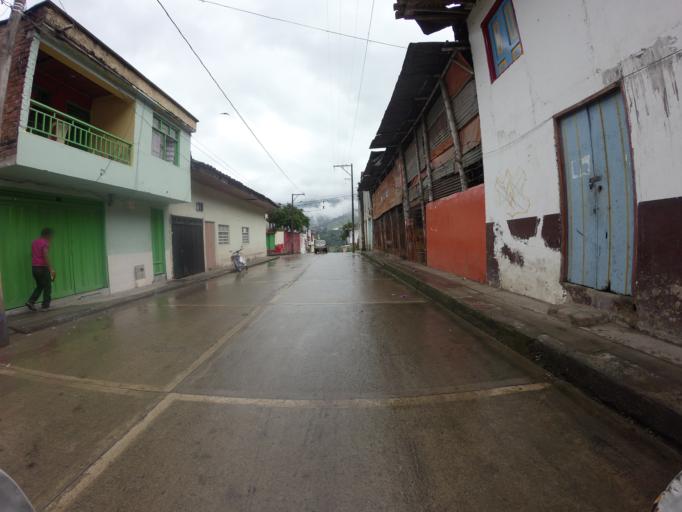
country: CO
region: Quindio
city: Genova
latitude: 4.2068
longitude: -75.7894
